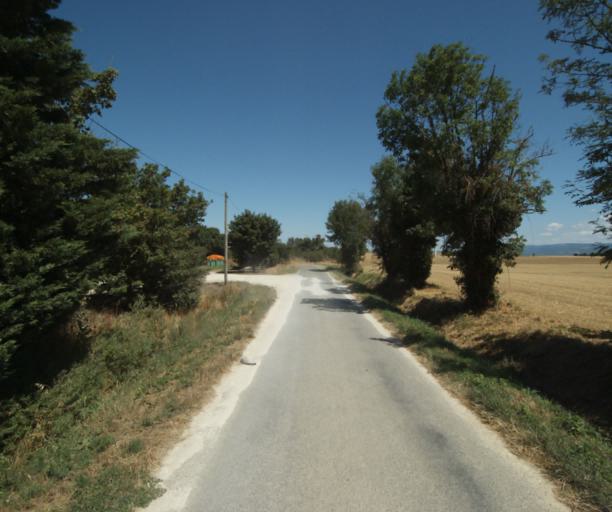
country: FR
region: Midi-Pyrenees
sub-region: Departement de la Haute-Garonne
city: Saint-Felix-Lauragais
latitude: 43.4557
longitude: 1.8978
